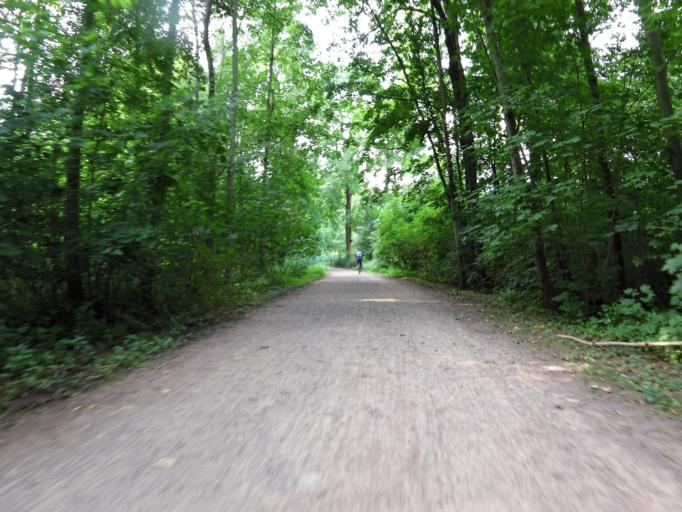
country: DE
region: Saxony
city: Leipzig
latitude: 51.3544
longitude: 12.3292
